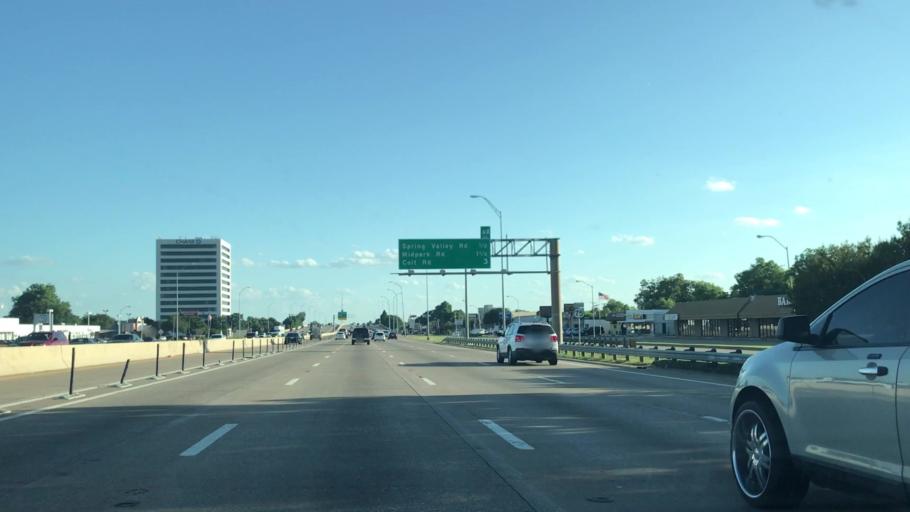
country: US
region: Texas
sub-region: Dallas County
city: Richardson
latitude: 32.9558
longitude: -96.7315
